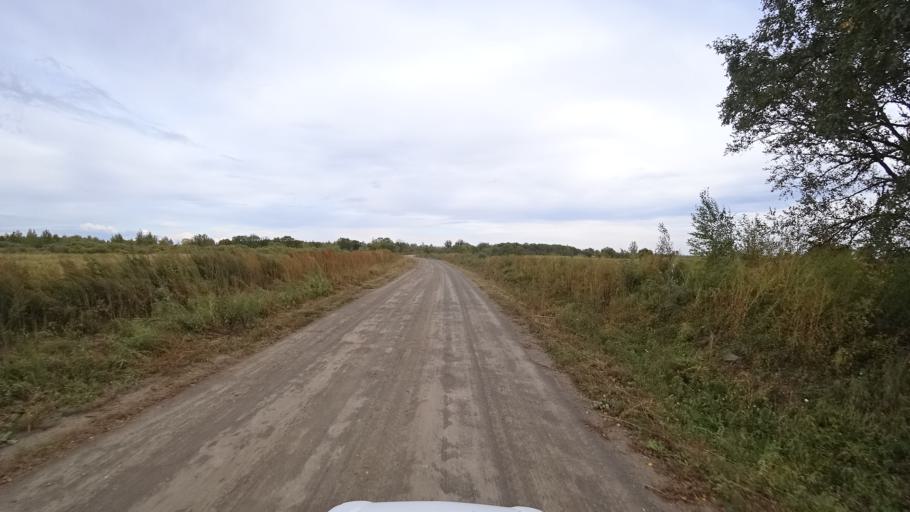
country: RU
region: Amur
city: Arkhara
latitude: 49.3532
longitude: 130.1449
